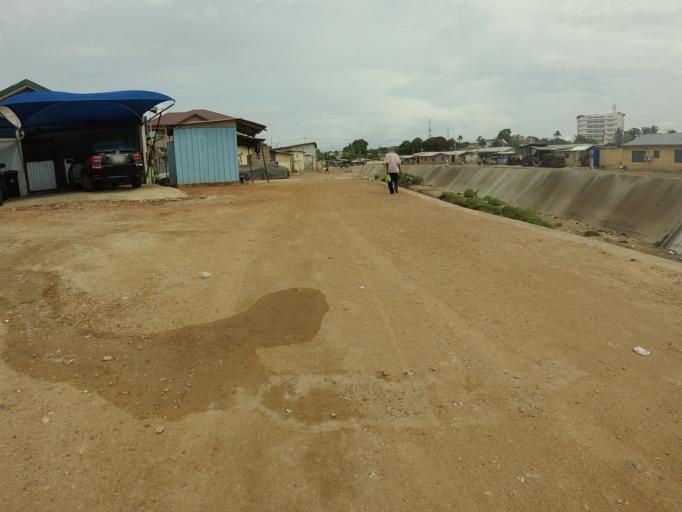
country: GH
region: Greater Accra
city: Accra
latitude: 5.6010
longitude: -0.2212
